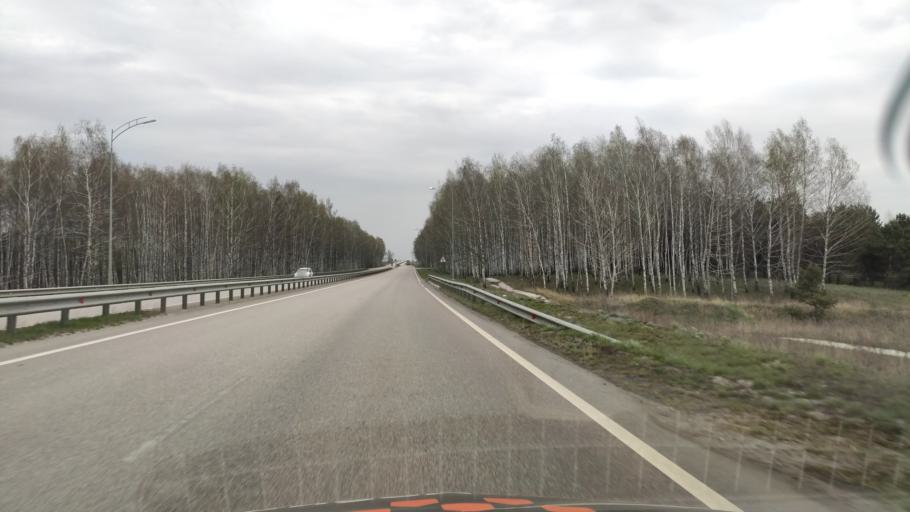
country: RU
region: Belgorod
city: Staryy Oskol
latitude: 51.4074
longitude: 37.8810
